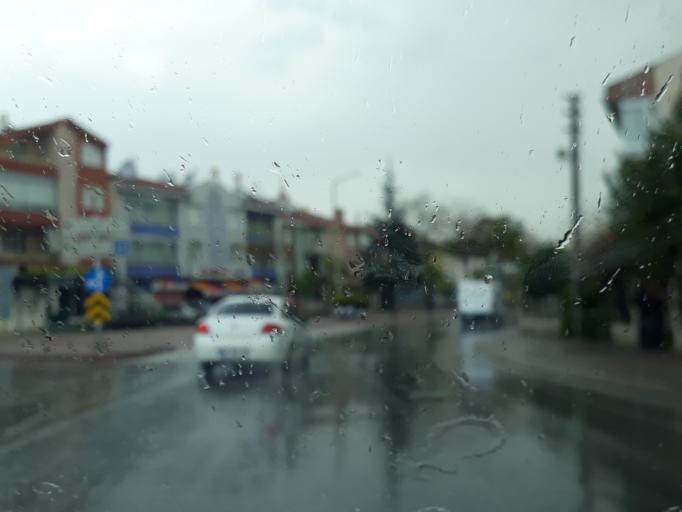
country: TR
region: Konya
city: Selcuklu
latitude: 37.9152
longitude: 32.4928
